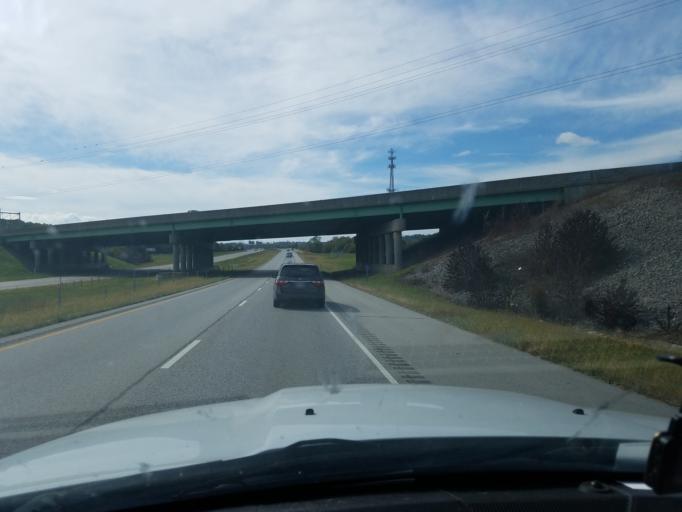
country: US
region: Indiana
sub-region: Floyd County
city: New Albany
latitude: 38.3368
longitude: -85.8171
